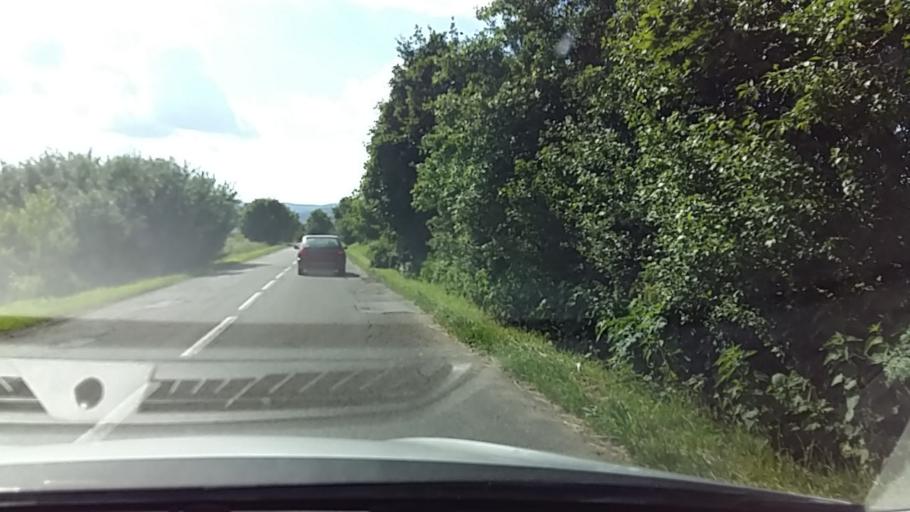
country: HU
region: Nograd
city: Diosjeno
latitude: 47.9057
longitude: 19.0629
